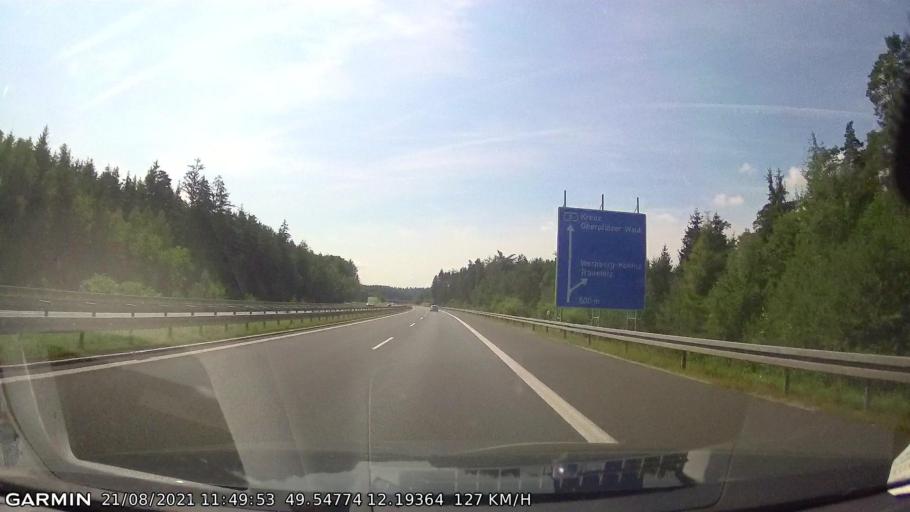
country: DE
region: Bavaria
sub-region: Upper Palatinate
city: Wernberg-Koblitz
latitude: 49.5476
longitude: 12.1936
